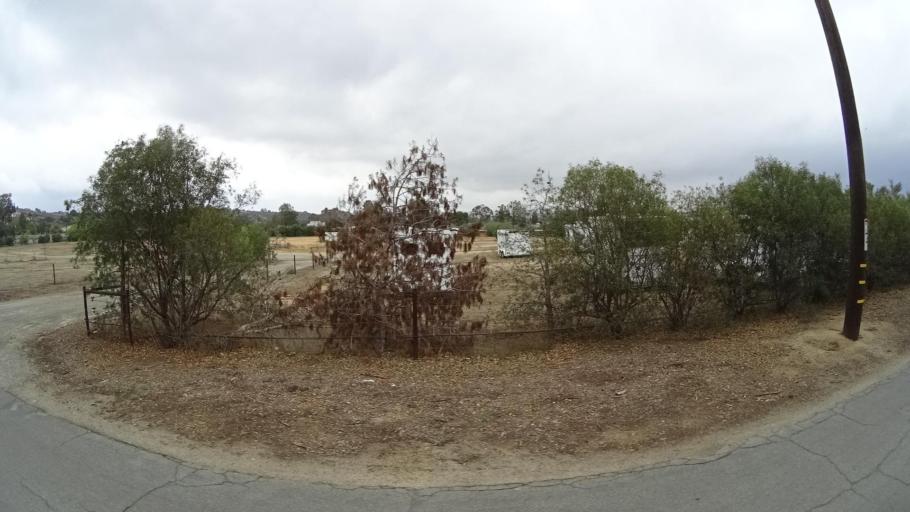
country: US
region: California
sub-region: San Diego County
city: Ramona
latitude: 33.0447
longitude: -116.9047
